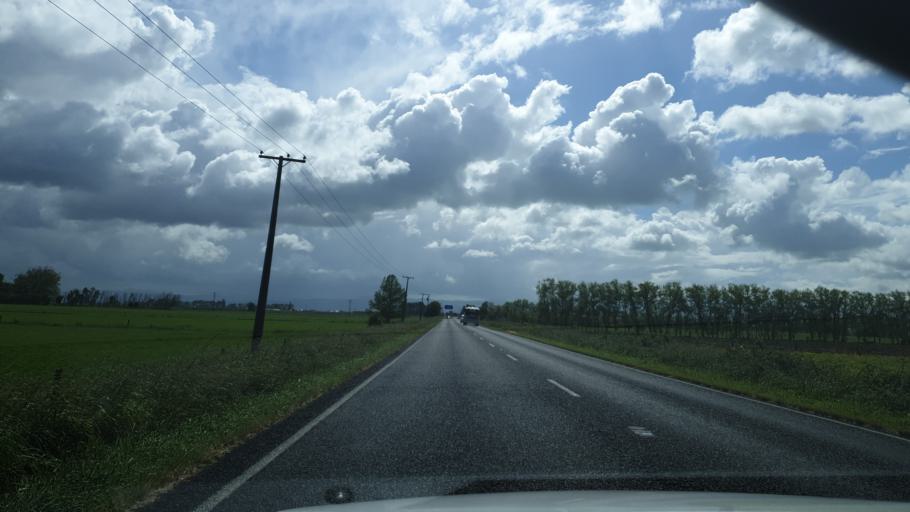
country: NZ
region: Waikato
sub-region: Hauraki District
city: Paeroa
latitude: -37.5123
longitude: 175.5171
